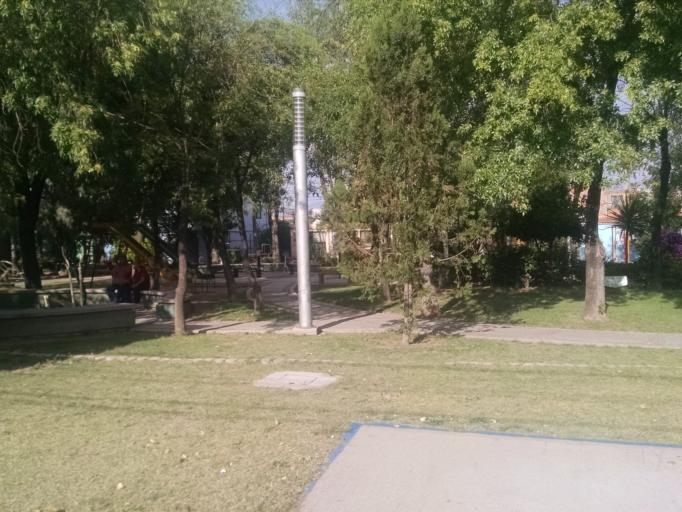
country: MX
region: Aguascalientes
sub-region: Aguascalientes
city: Aguascalientes
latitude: 21.8829
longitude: -102.3123
